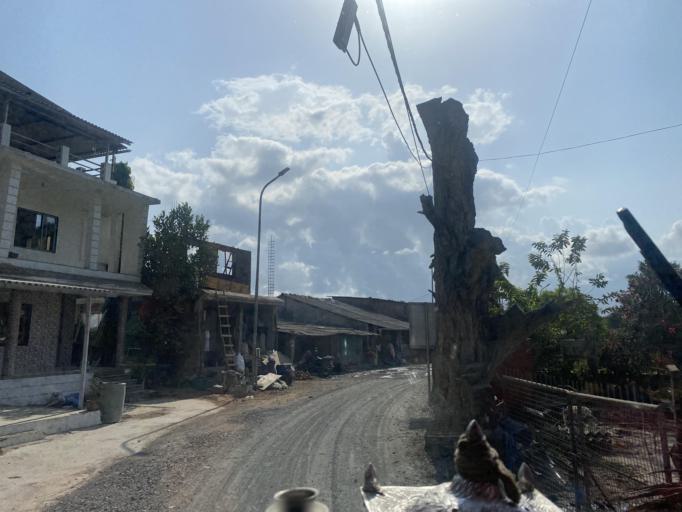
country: IN
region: Daman and Diu
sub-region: Daman District
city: Daman
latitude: 20.3774
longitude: 72.8268
